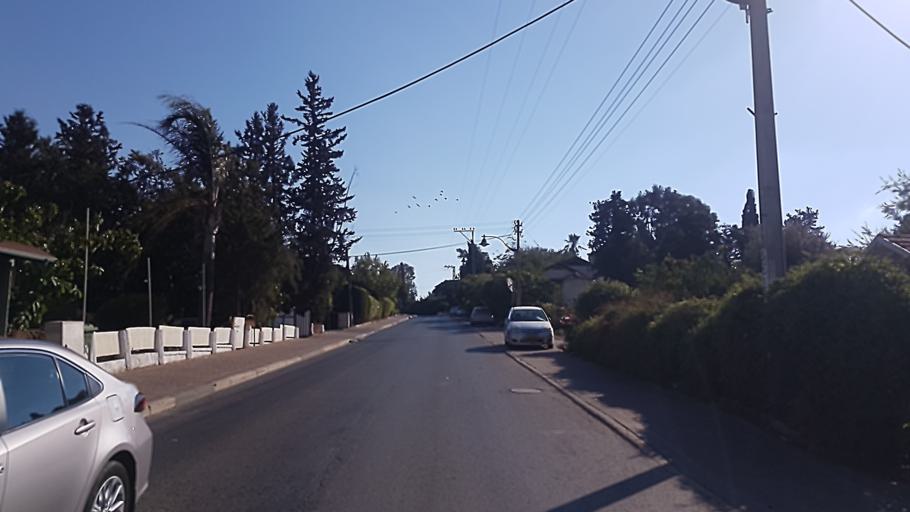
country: IL
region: Central District
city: Kfar Saba
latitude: 32.2087
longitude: 34.9043
